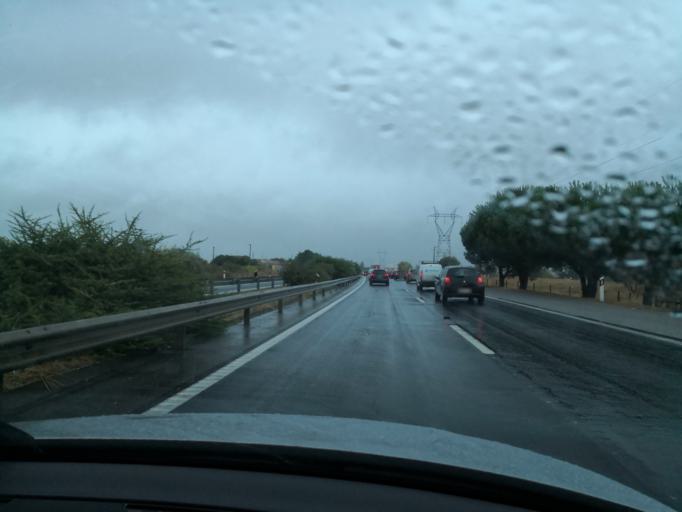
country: PT
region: Setubal
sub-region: Moita
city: Moita
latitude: 38.6667
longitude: -8.9546
